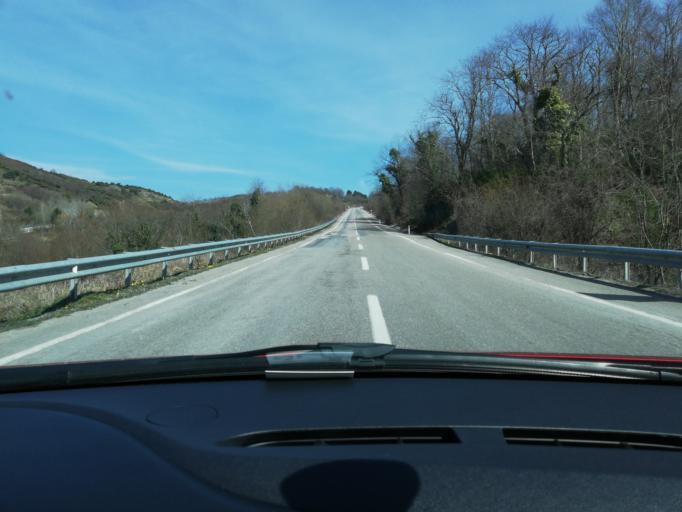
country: TR
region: Bartin
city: Amasra
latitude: 41.7243
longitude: 32.4032
